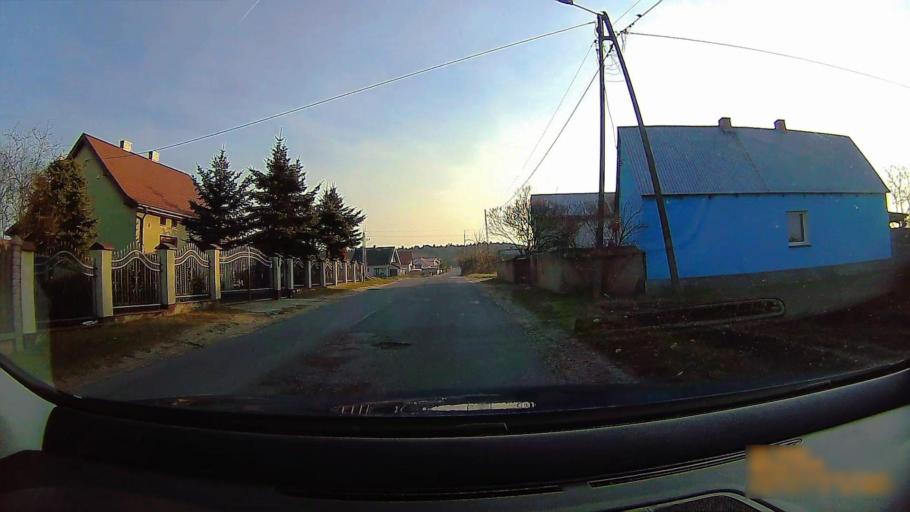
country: PL
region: Greater Poland Voivodeship
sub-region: Konin
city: Konin
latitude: 52.1881
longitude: 18.3322
